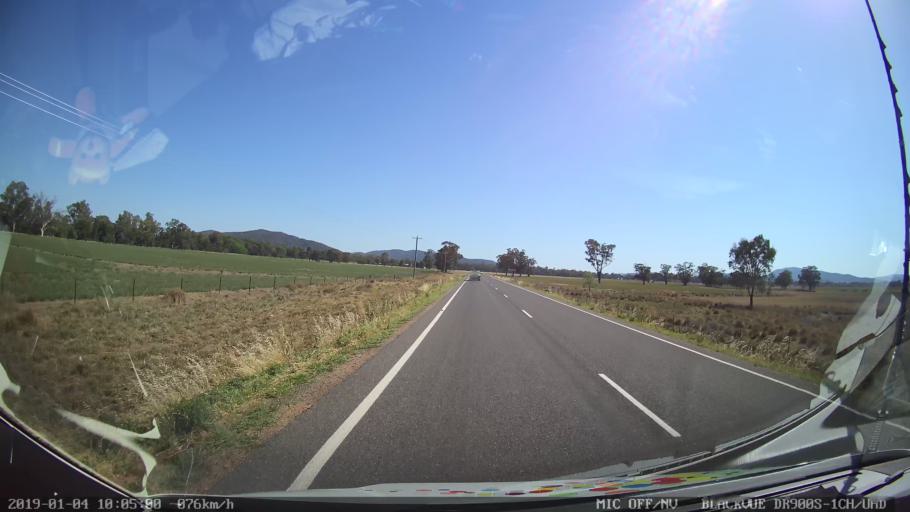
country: AU
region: New South Wales
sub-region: Cabonne
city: Canowindra
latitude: -33.4468
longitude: 148.3634
